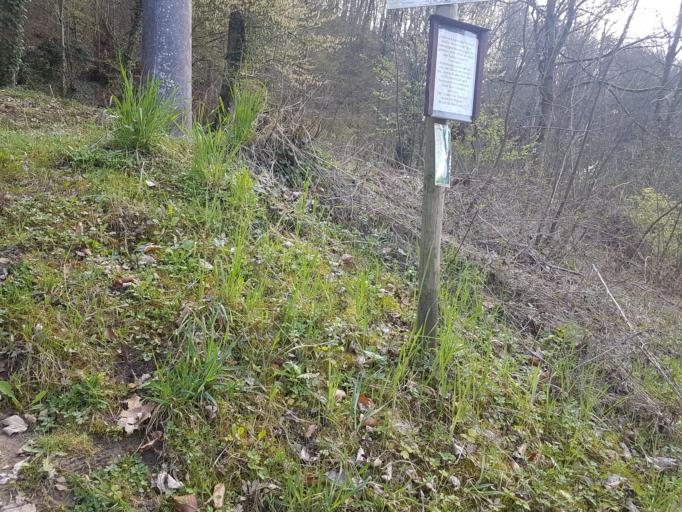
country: DE
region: Baden-Wuerttemberg
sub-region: Regierungsbezirk Stuttgart
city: Jagsthausen
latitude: 49.3272
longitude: 9.5036
